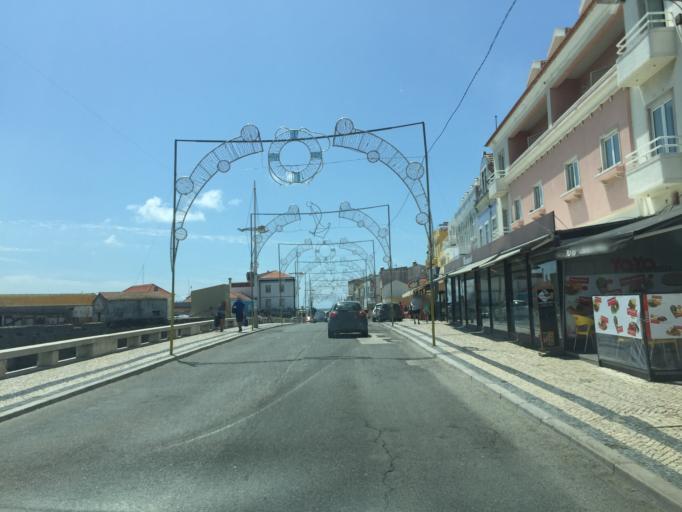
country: PT
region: Leiria
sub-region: Peniche
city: Peniche
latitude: 39.3560
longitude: -9.3785
